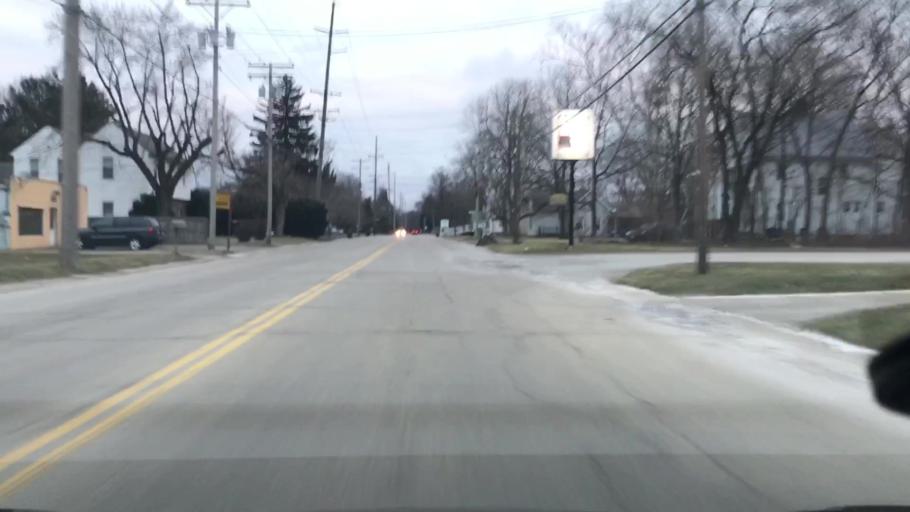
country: US
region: Ohio
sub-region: Clark County
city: Springfield
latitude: 39.9372
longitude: -83.7609
